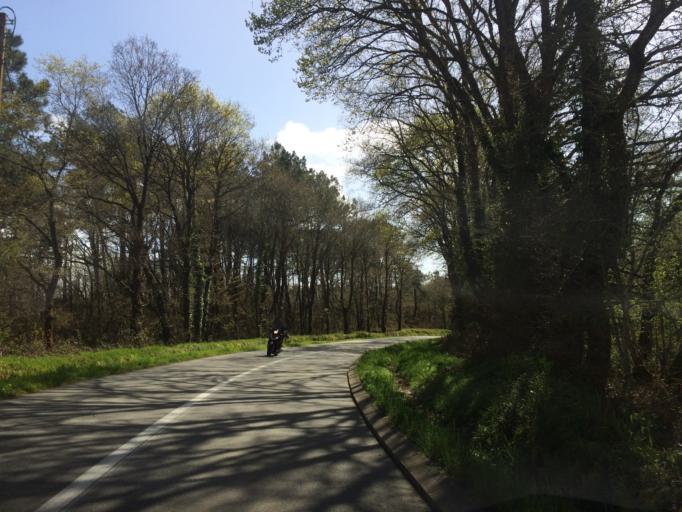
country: FR
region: Brittany
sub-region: Departement du Morbihan
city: Ploemel
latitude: 47.6372
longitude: -3.0474
